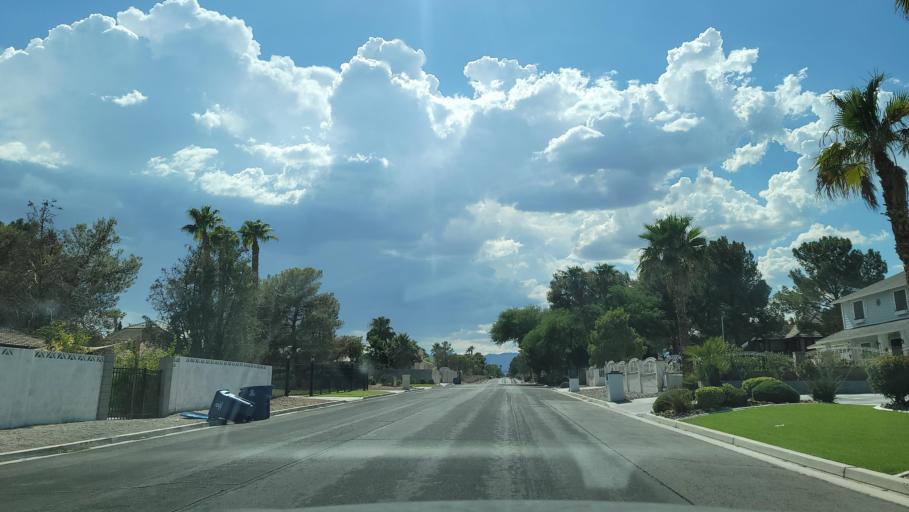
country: US
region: Nevada
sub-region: Clark County
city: Spring Valley
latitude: 36.1313
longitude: -115.2456
